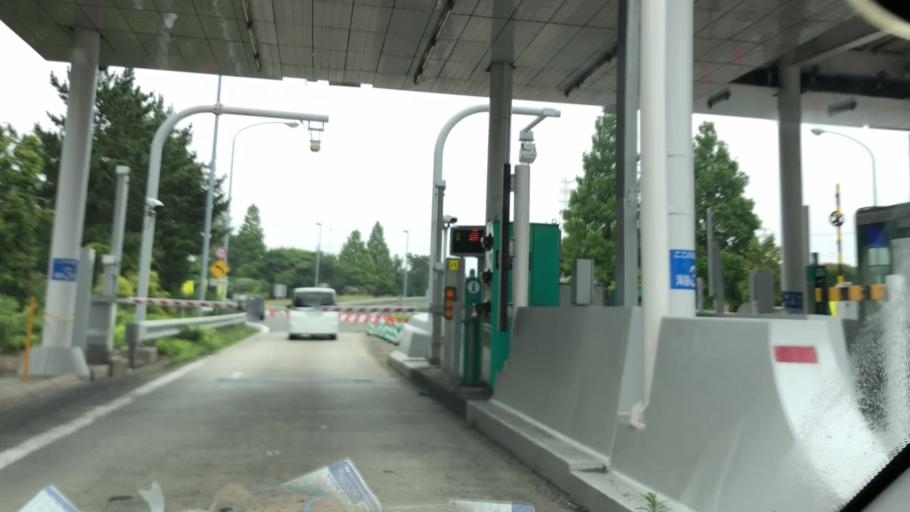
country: JP
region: Miyagi
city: Rifu
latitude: 38.2806
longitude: 140.9905
